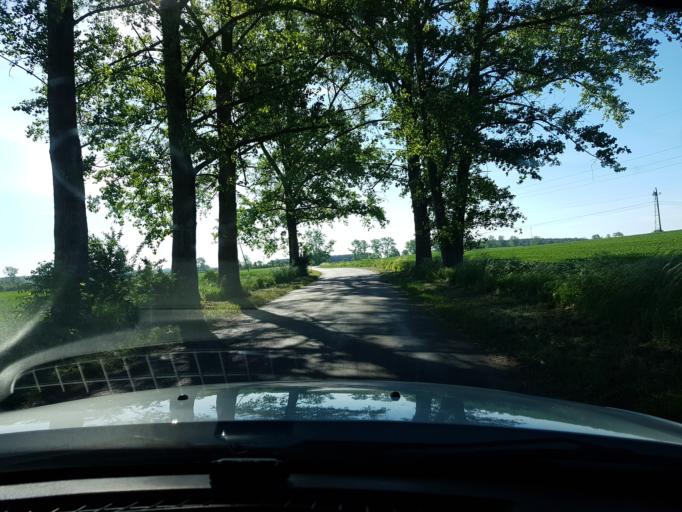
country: PL
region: West Pomeranian Voivodeship
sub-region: Powiat gryfinski
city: Gryfino
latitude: 53.2144
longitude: 14.6017
